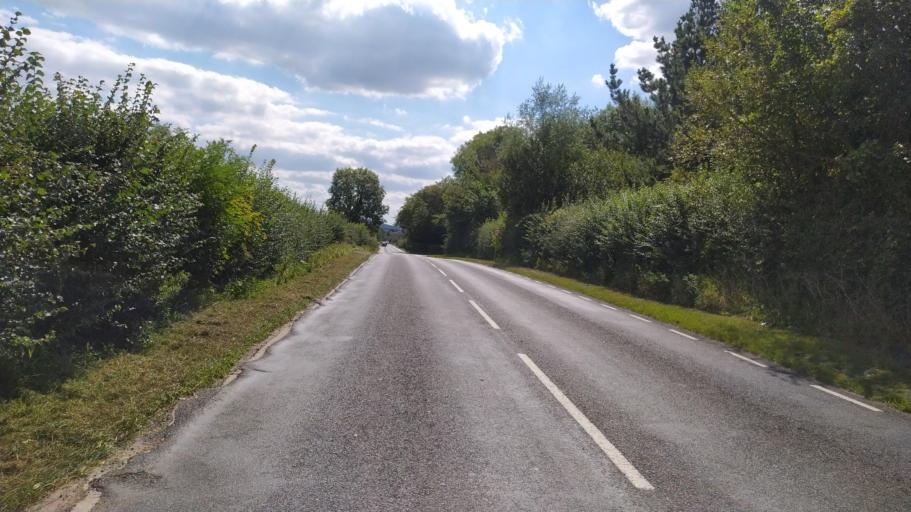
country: GB
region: England
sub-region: Dorset
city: Gillingham
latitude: 51.0537
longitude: -2.2841
